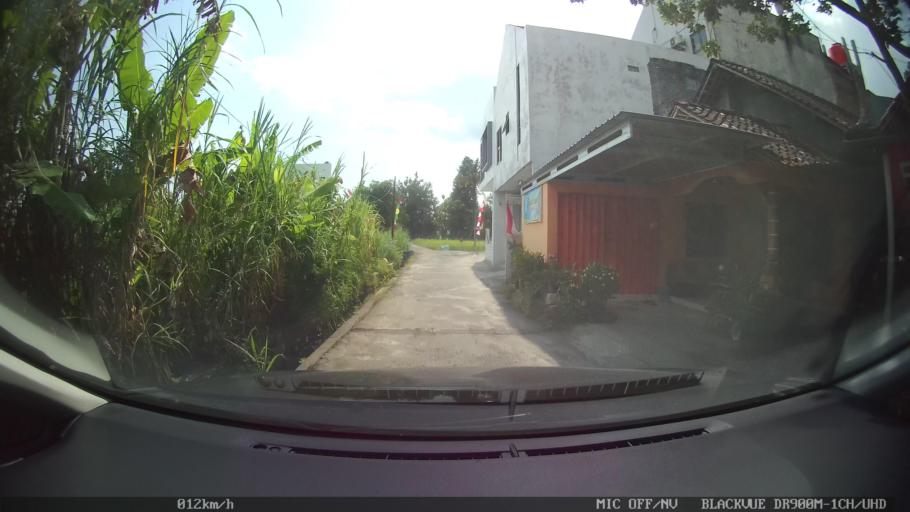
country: ID
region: Daerah Istimewa Yogyakarta
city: Kasihan
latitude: -7.8120
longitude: 110.3292
